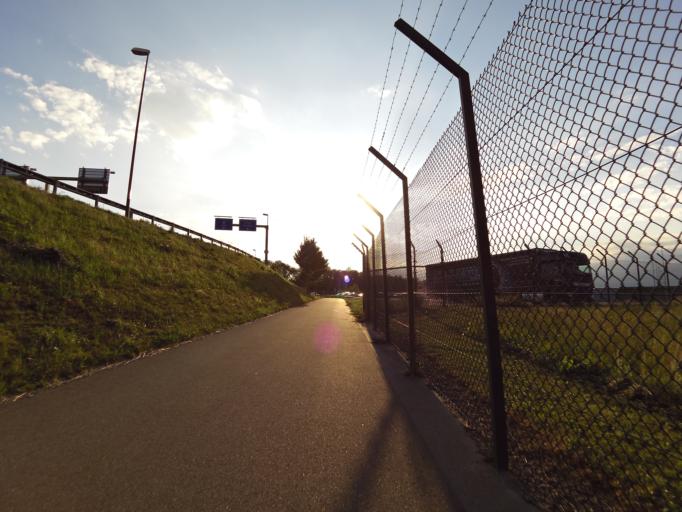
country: CH
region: Zurich
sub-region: Bezirk Buelach
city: Glattbrugg / Rohr/Platten-Balsberg
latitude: 47.4389
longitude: 8.5607
